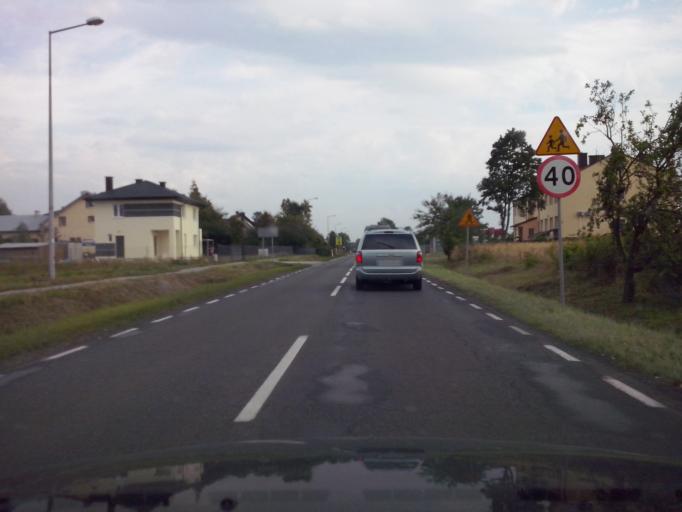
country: PL
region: Lublin Voivodeship
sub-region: Powiat bilgorajski
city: Bilgoraj
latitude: 50.5074
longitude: 22.7200
